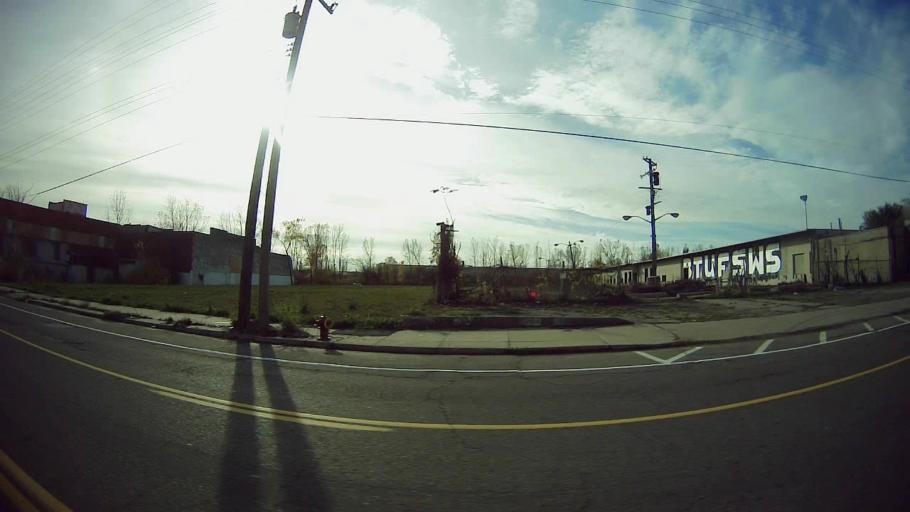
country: US
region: Michigan
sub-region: Wayne County
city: Highland Park
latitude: 42.4031
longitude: -83.1220
